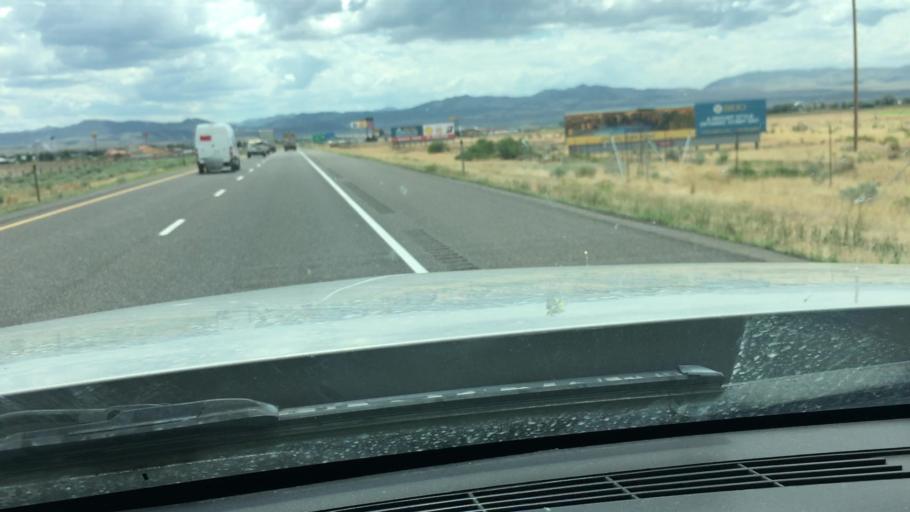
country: US
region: Utah
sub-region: Beaver County
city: Beaver
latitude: 38.3029
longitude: -112.6525
